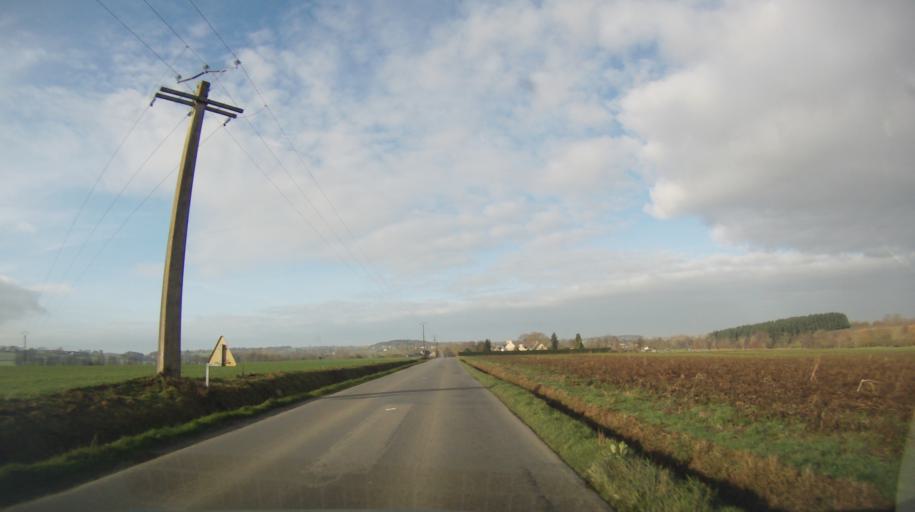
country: FR
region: Brittany
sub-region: Departement d'Ille-et-Vilaine
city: Corps-Nuds
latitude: 47.9473
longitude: -1.5864
